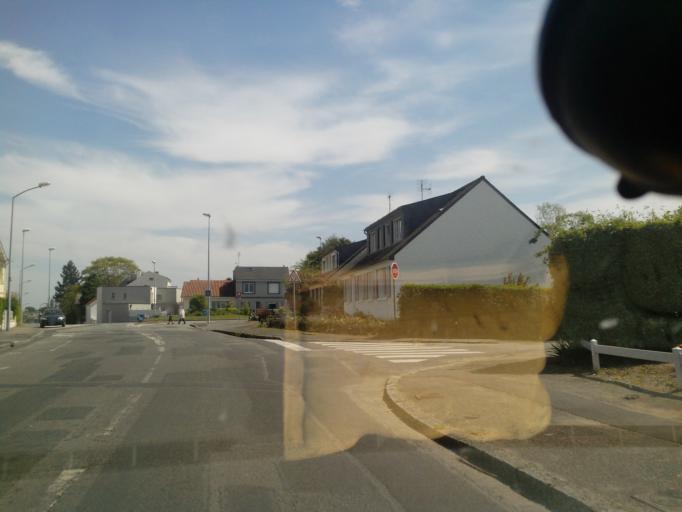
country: FR
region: Pays de la Loire
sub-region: Departement de la Loire-Atlantique
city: Orvault
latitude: 47.2503
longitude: -1.5879
